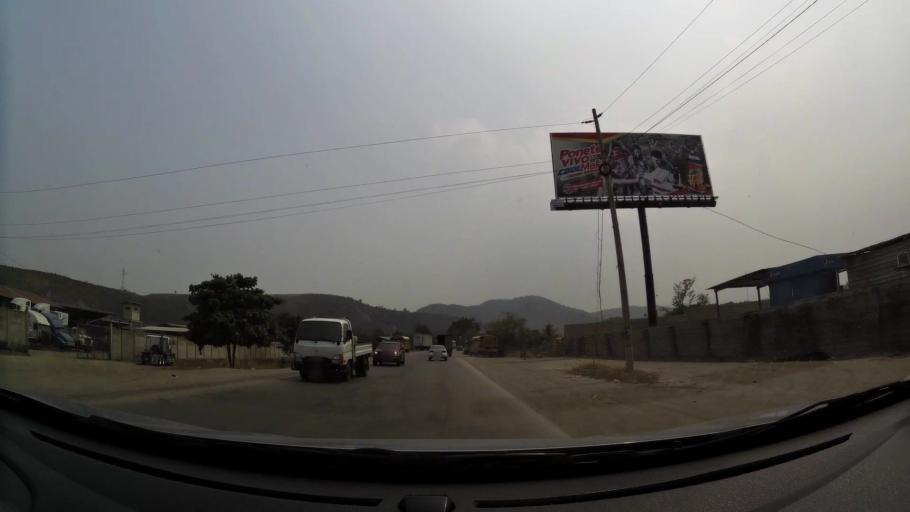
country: HN
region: Cortes
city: Chotepe
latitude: 15.4642
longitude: -87.9632
